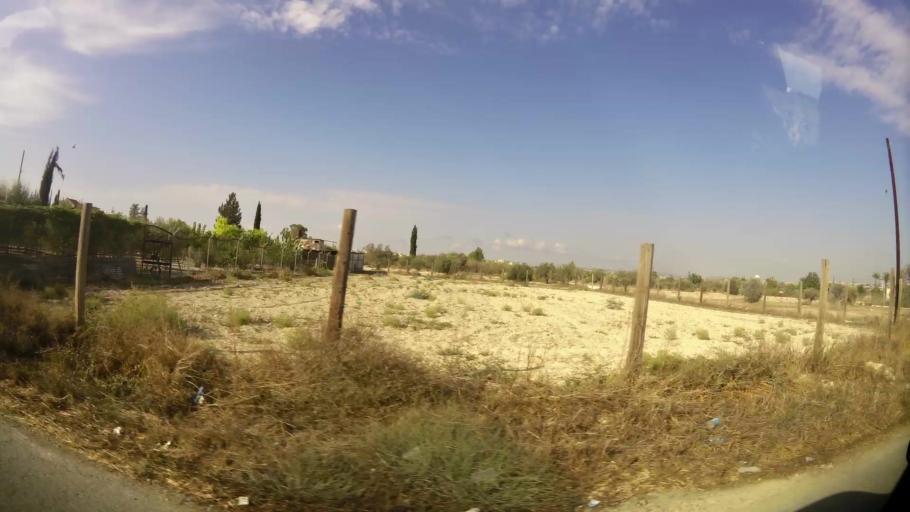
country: CY
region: Larnaka
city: Aradippou
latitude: 34.9563
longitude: 33.6084
